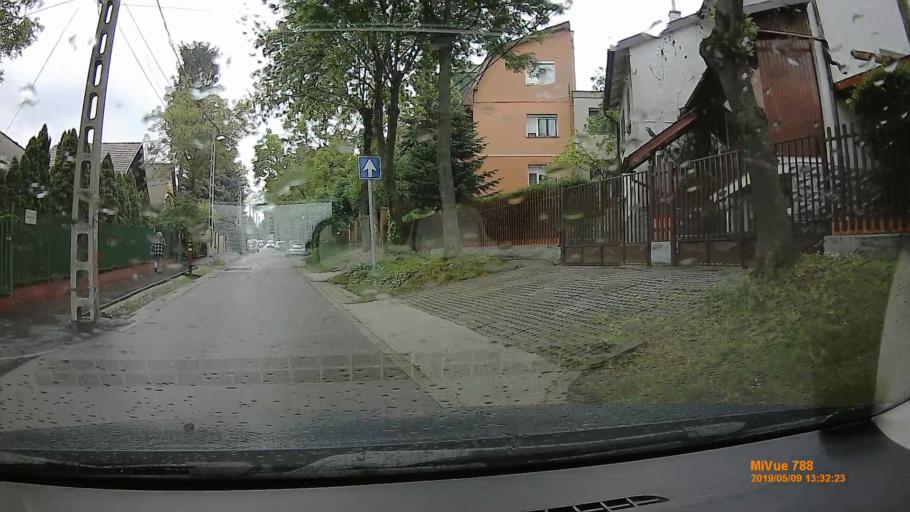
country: HU
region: Pest
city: Csomor
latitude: 47.5337
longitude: 19.2017
